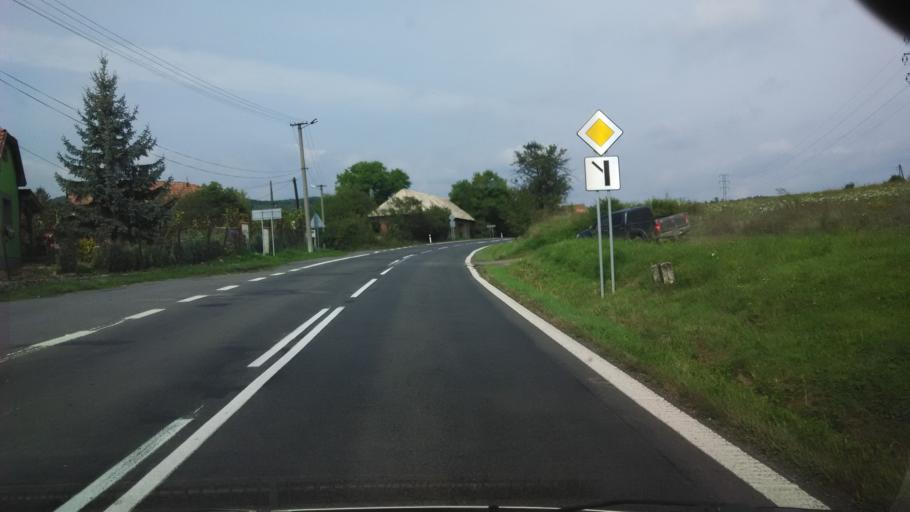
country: SK
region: Banskobystricky
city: Krupina
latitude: 48.3052
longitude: 19.0272
